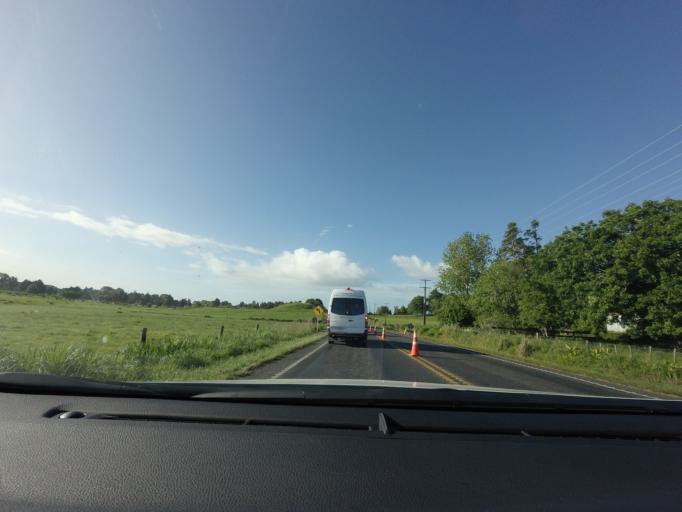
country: NZ
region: Waikato
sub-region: Hauraki District
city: Ngatea
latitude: -37.4697
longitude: 175.5097
